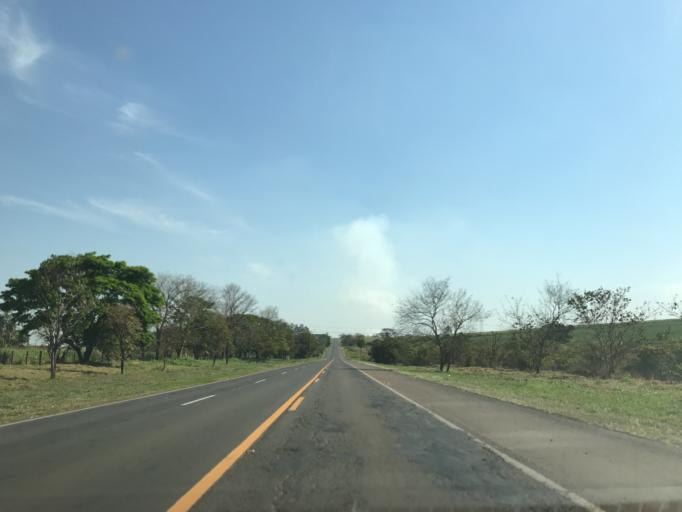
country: BR
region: Sao Paulo
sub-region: Penapolis
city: Penapolis
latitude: -21.3459
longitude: -50.0518
